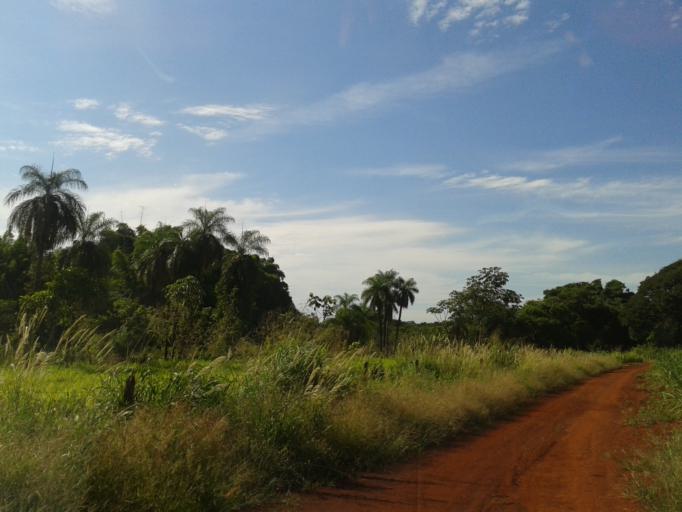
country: BR
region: Minas Gerais
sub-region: Centralina
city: Centralina
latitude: -18.6301
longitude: -49.2577
